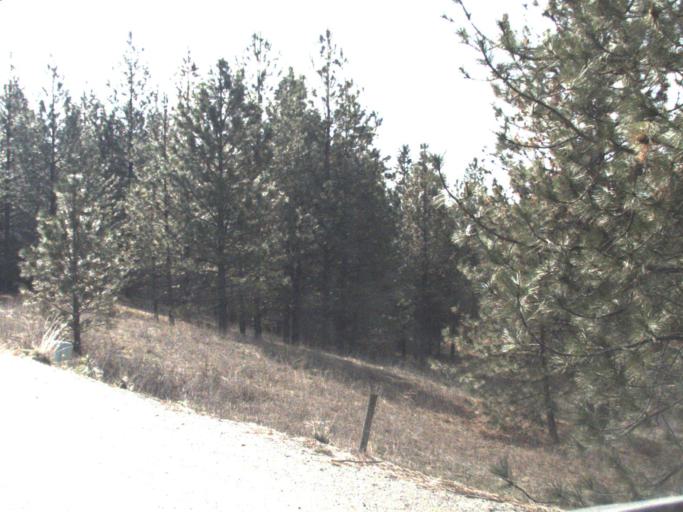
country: US
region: Washington
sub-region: Stevens County
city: Colville
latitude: 48.5081
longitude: -117.7220
